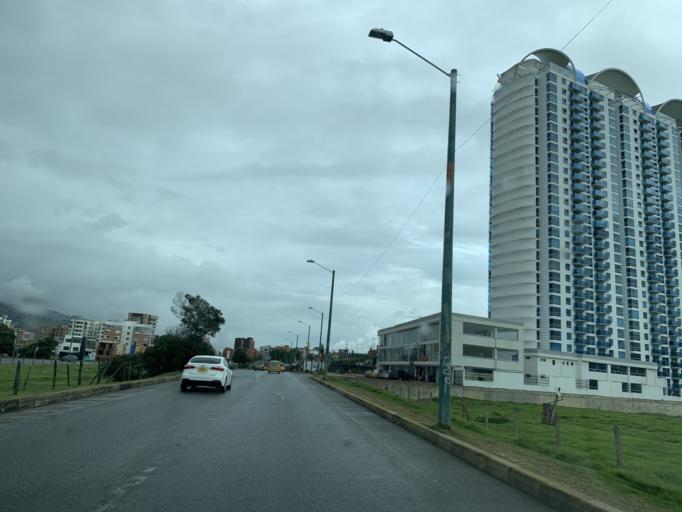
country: CO
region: Boyaca
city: Tunja
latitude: 5.5384
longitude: -73.3517
